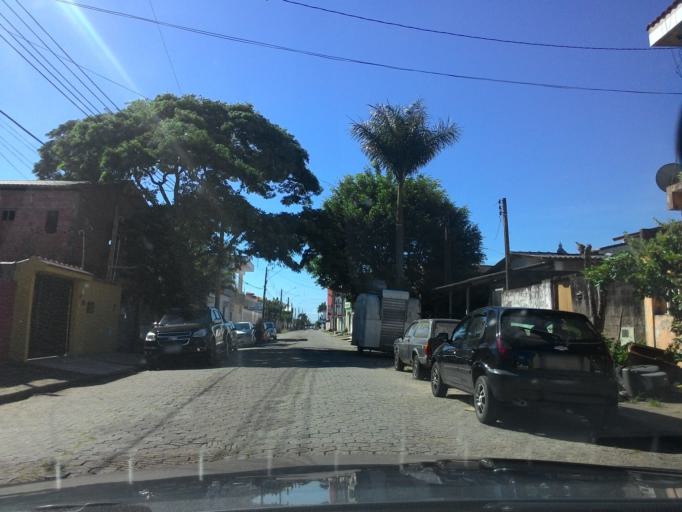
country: BR
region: Sao Paulo
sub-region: Iguape
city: Iguape
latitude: -24.7024
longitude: -47.5590
